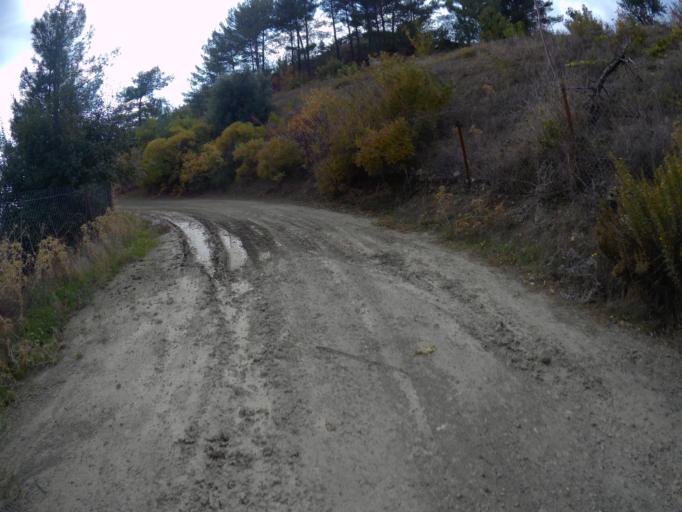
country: CY
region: Lefkosia
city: Kakopetria
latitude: 34.9172
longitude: 32.8135
